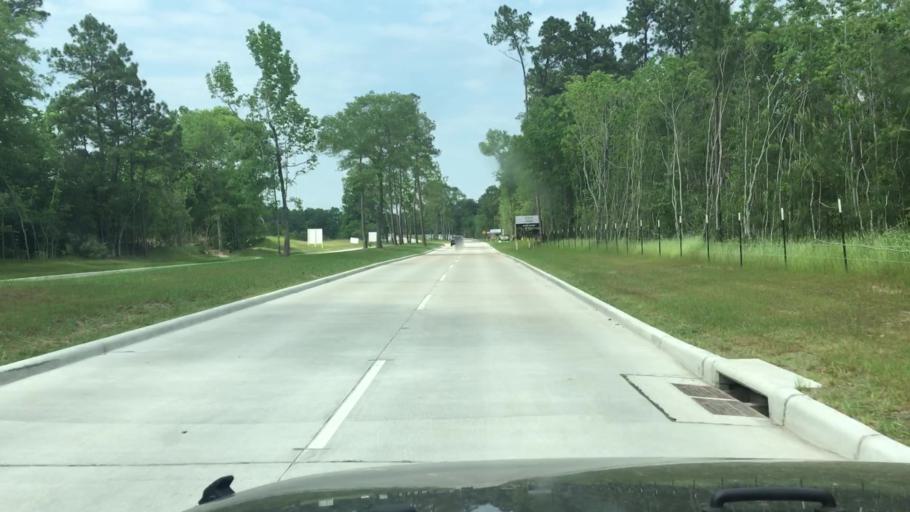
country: US
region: Texas
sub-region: Harris County
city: Atascocita
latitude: 29.9570
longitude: -95.2099
